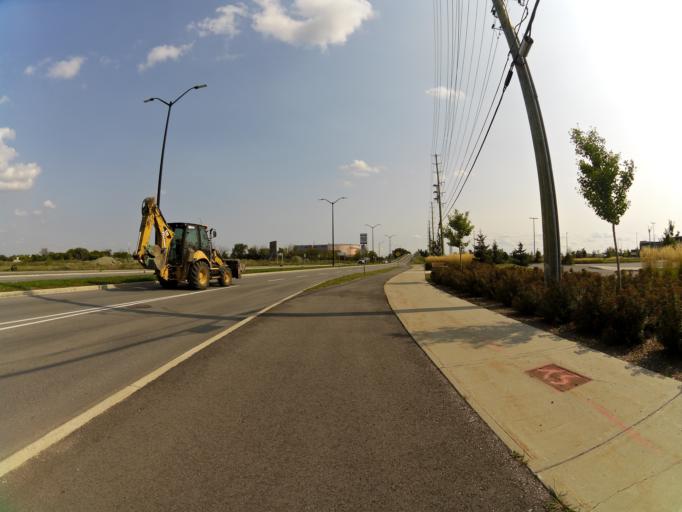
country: CA
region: Ontario
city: Bells Corners
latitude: 45.3006
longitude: -75.9356
